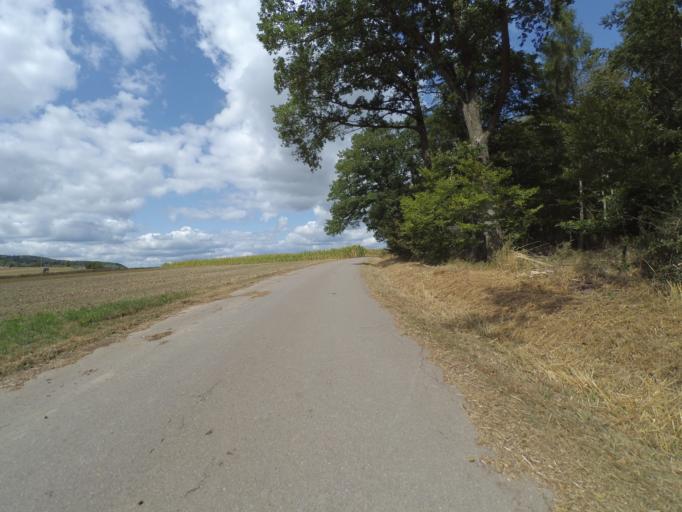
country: LU
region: Grevenmacher
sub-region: Canton de Grevenmacher
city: Flaxweiler
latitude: 49.6712
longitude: 6.3477
